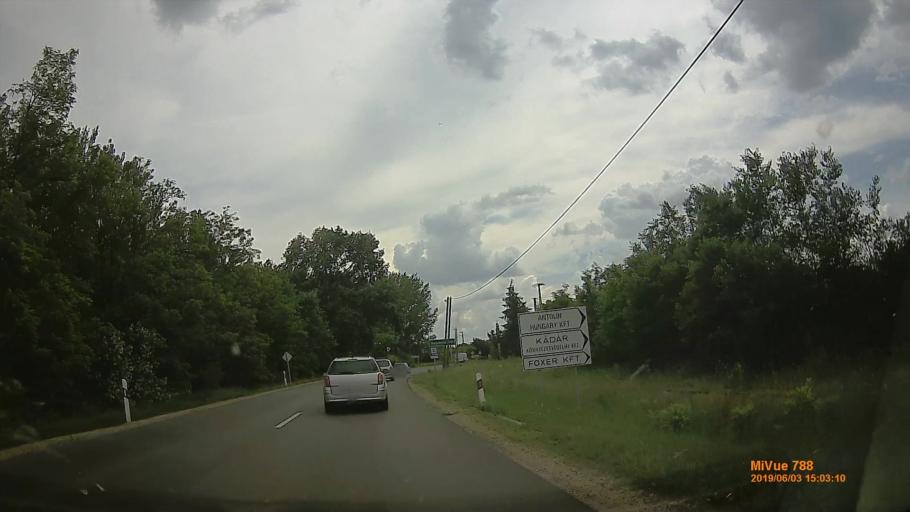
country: HU
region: Bacs-Kiskun
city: Helvecia
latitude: 46.8363
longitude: 19.6521
